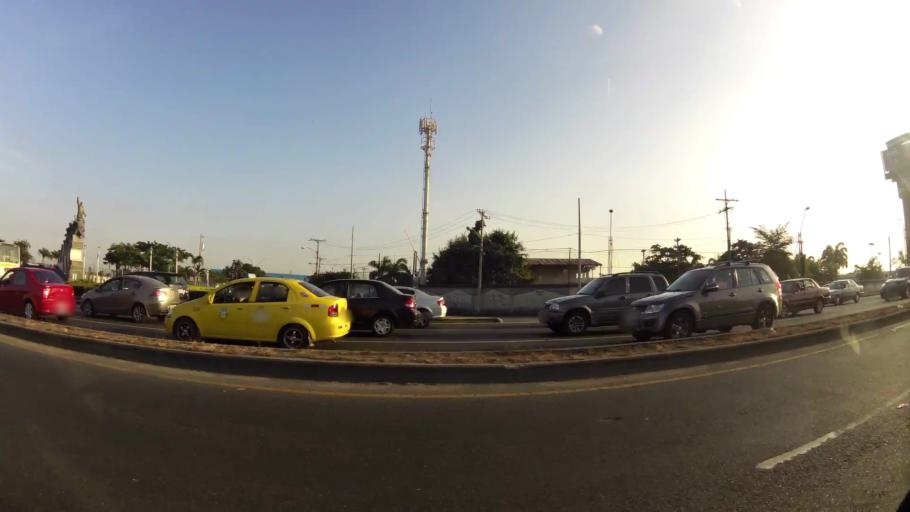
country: EC
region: Guayas
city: Eloy Alfaro
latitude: -2.1549
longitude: -79.8778
